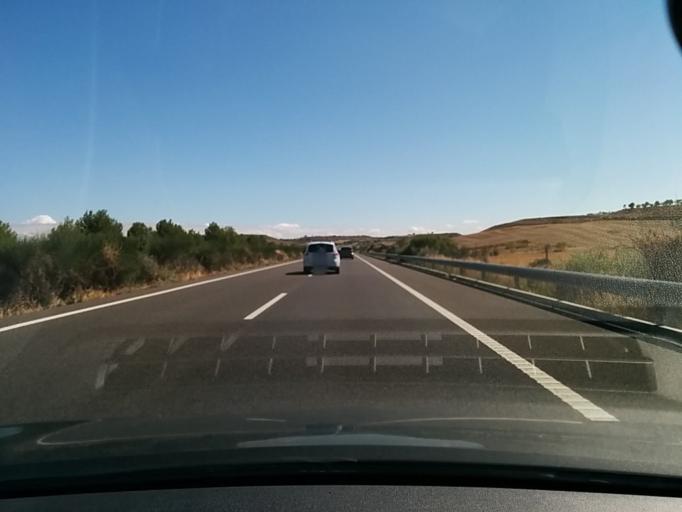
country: ES
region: Aragon
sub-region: Provincia de Huesca
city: Almudebar
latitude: 42.0497
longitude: -0.5542
